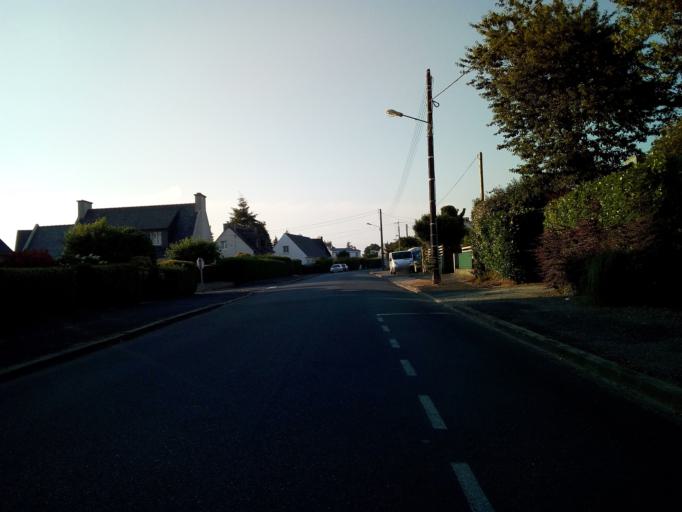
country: FR
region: Brittany
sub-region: Departement du Finistere
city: Landivisiau
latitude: 48.5002
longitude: -4.0786
